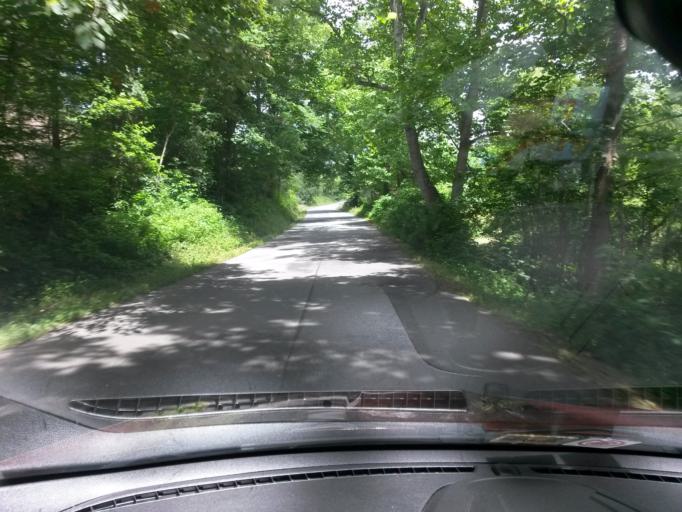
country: US
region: West Virginia
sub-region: Monroe County
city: Union
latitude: 37.5073
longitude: -80.5774
